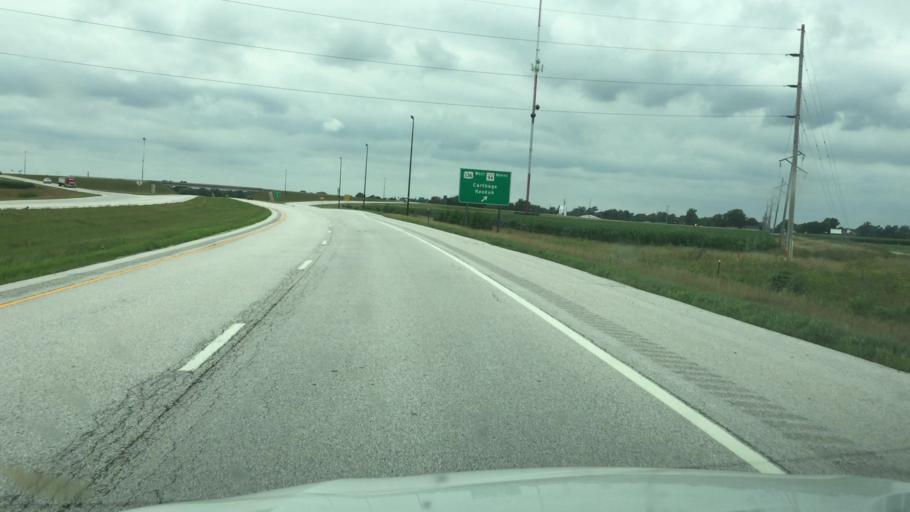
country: US
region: Illinois
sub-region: Hancock County
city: Carthage
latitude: 40.4157
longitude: -91.1068
